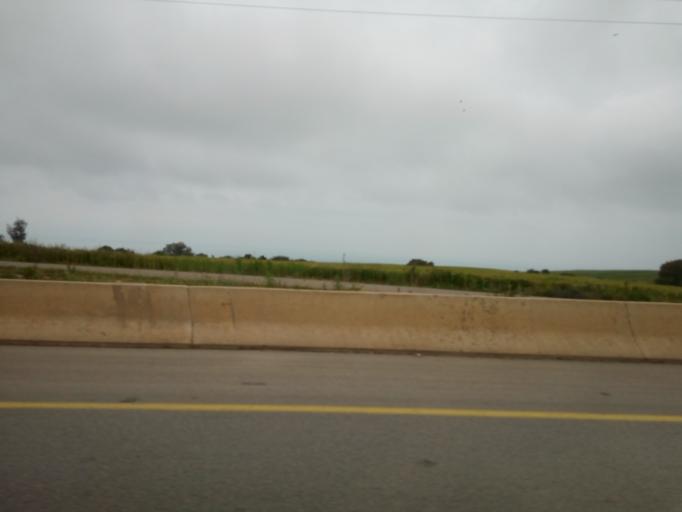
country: DZ
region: Tipaza
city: Bou Ismail
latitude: 36.6010
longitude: 2.6466
